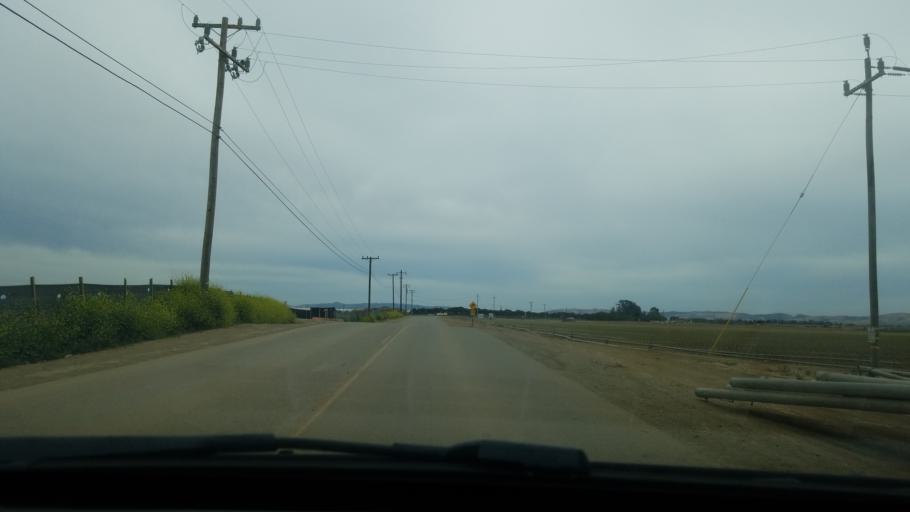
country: US
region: California
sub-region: San Luis Obispo County
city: Nipomo
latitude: 34.9980
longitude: -120.5157
